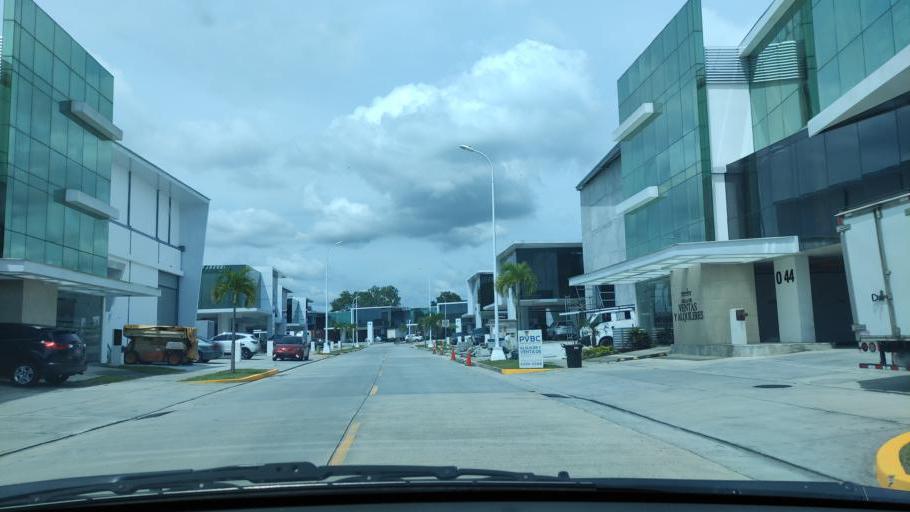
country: PA
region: Panama
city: Panama
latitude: 9.0101
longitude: -79.4882
